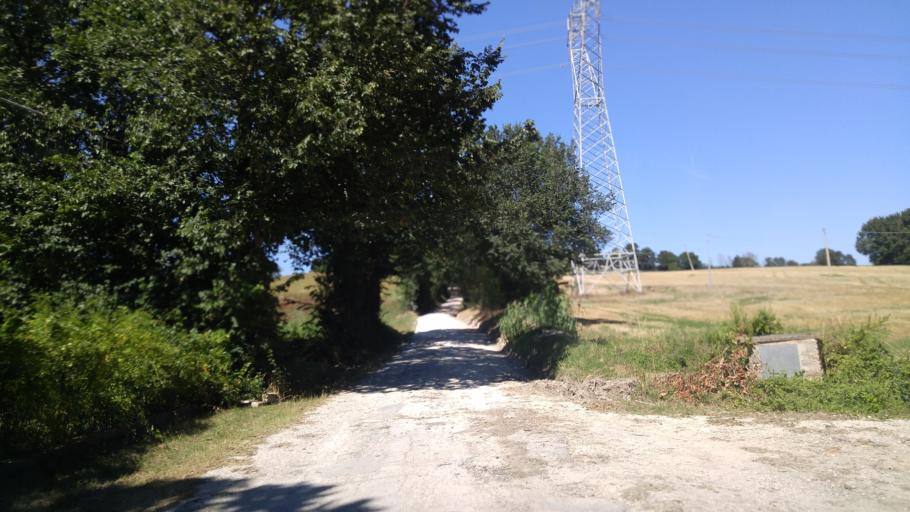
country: IT
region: The Marches
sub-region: Provincia di Pesaro e Urbino
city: Mombaroccio
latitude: 43.8201
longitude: 12.8860
